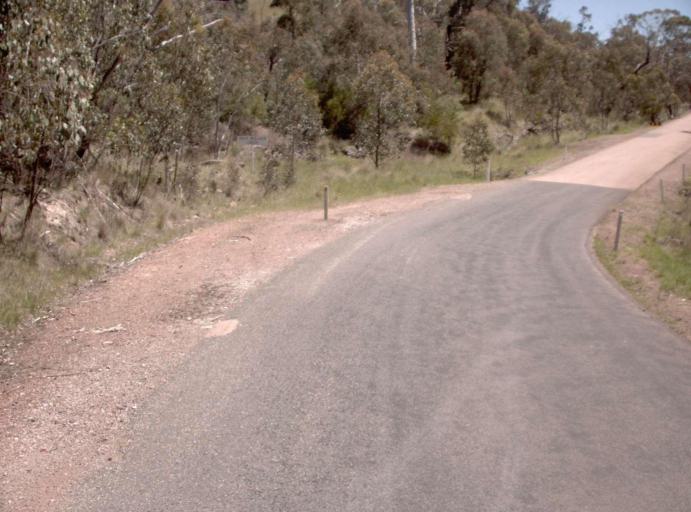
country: AU
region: New South Wales
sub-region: Snowy River
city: Jindabyne
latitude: -37.1067
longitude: 148.2501
